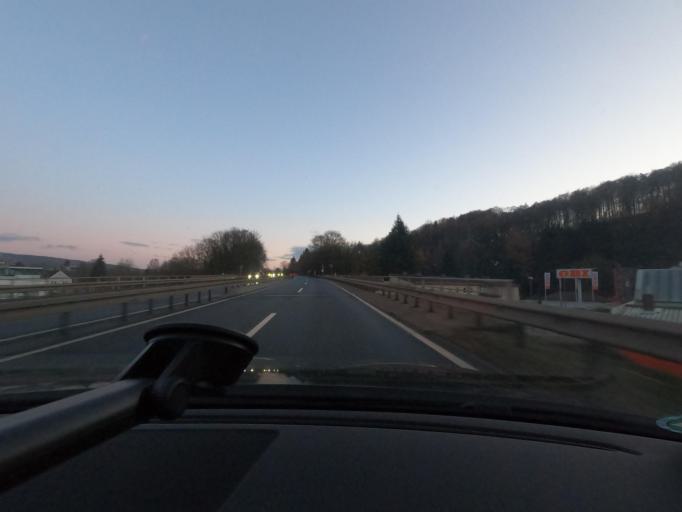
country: DE
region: Lower Saxony
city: Osterode am Harz
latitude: 51.7267
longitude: 10.2413
